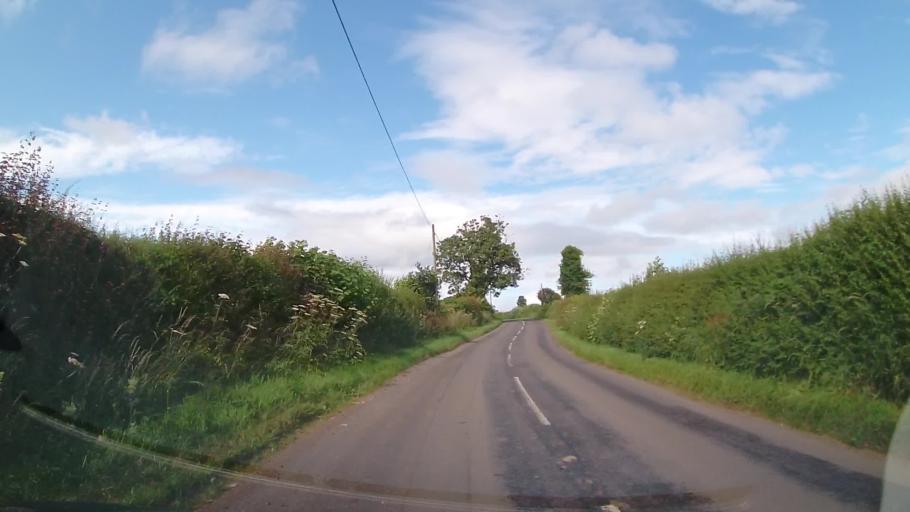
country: GB
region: England
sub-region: Shropshire
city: Petton
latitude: 52.8117
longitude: -2.8237
